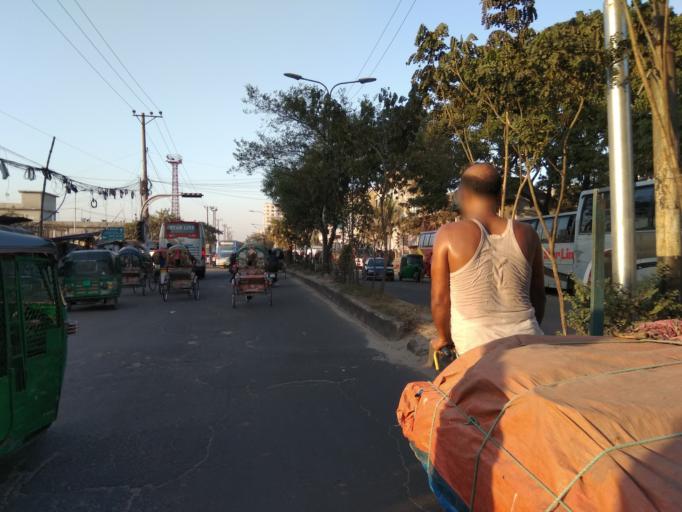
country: BD
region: Dhaka
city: Paltan
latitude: 23.7245
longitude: 90.4287
